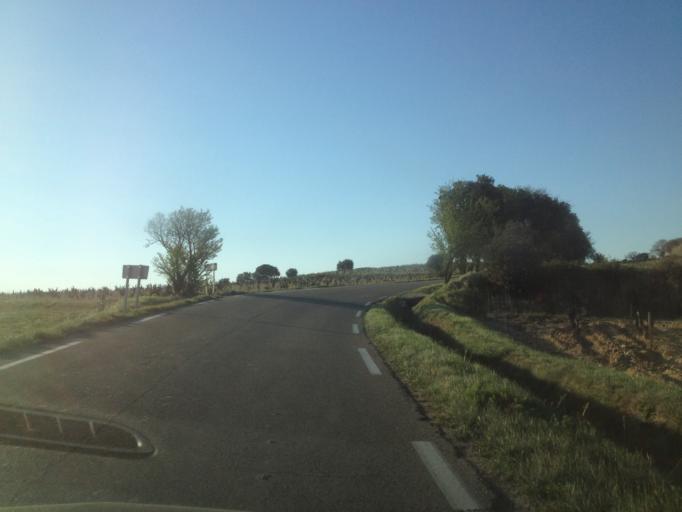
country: FR
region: Provence-Alpes-Cote d'Azur
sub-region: Departement du Vaucluse
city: Chateauneuf-du-Pape
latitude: 44.0875
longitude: 4.8304
